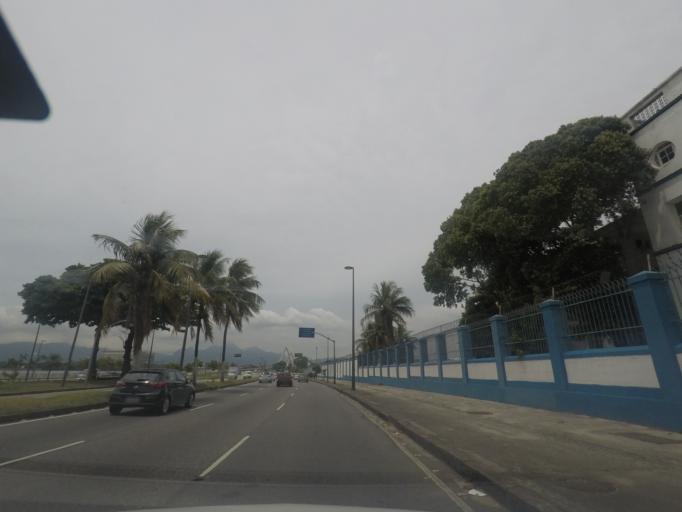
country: BR
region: Rio de Janeiro
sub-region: Rio De Janeiro
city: Rio de Janeiro
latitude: -22.8284
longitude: -43.2354
